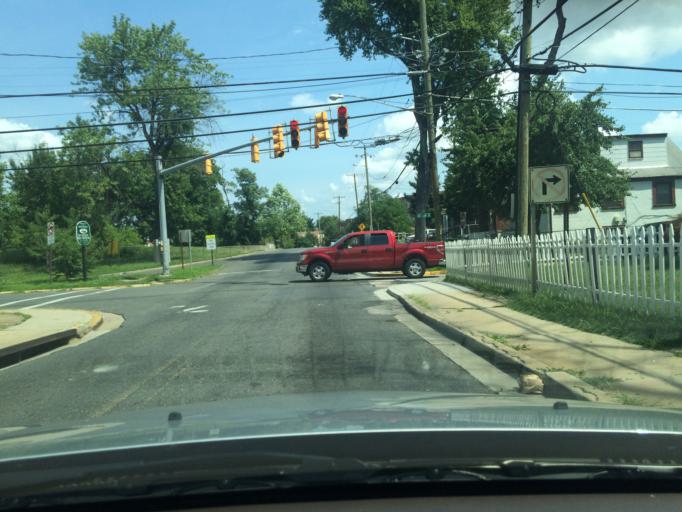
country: US
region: Maryland
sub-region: Prince George's County
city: Mount Rainier
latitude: 38.9478
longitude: -76.9622
